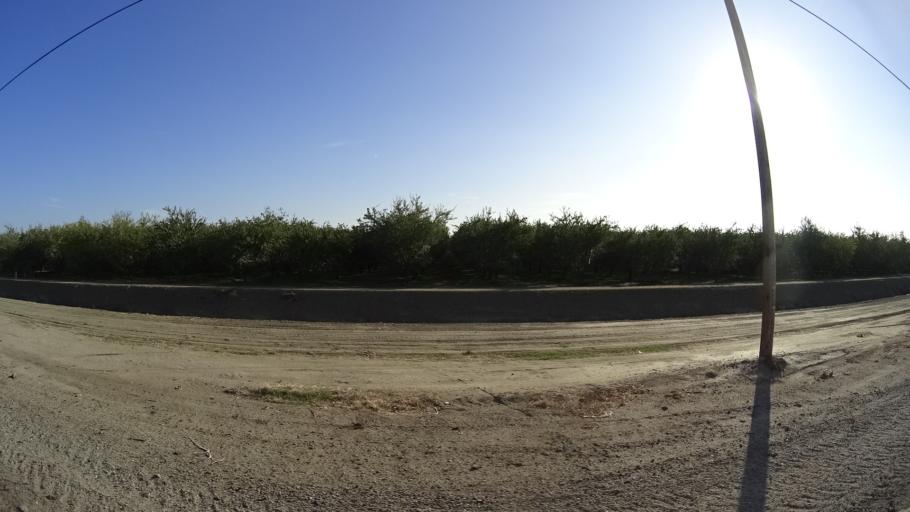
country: US
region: California
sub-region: Kern County
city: Rosedale
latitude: 35.2962
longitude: -119.1484
